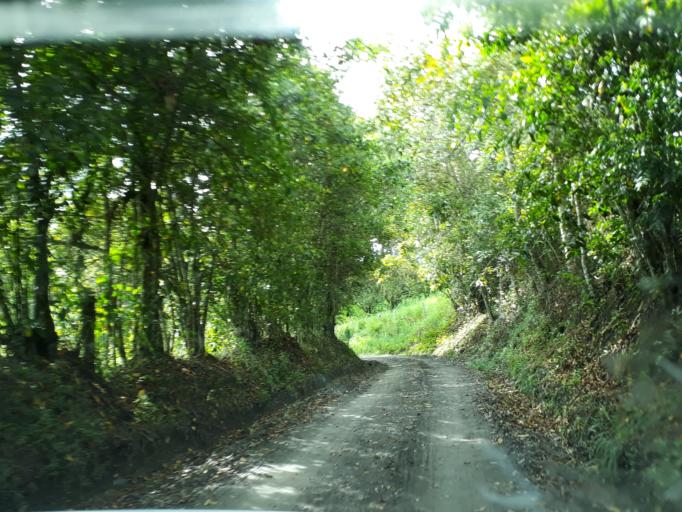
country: CO
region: Cundinamarca
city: Pacho
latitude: 5.1818
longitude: -74.2505
